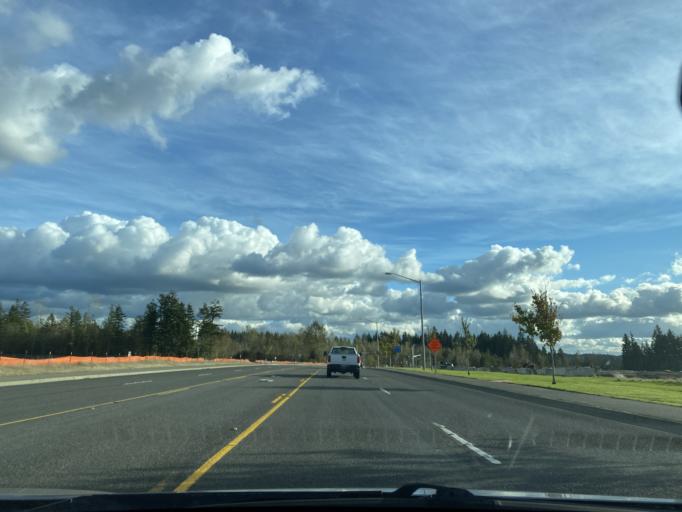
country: US
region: Washington
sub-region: Pierce County
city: South Hill
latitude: 47.0973
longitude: -122.2649
